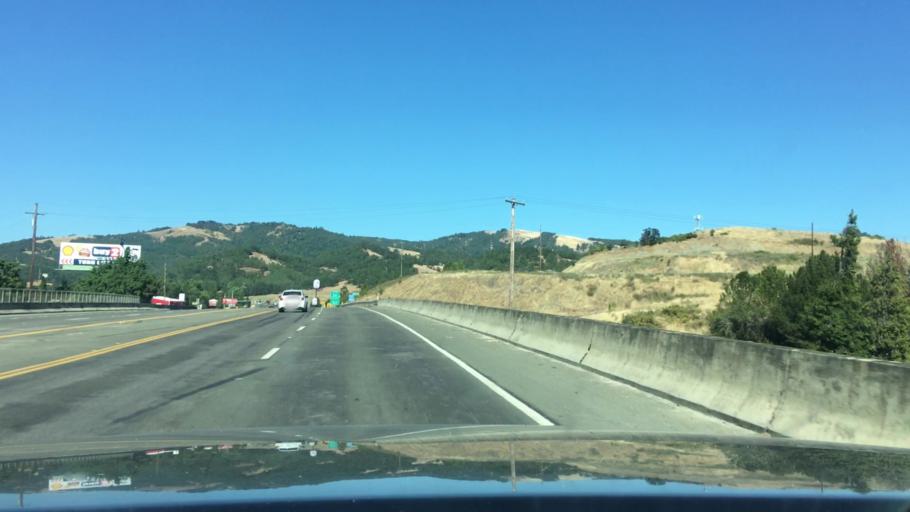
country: US
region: Oregon
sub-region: Douglas County
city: Green
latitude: 43.1475
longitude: -123.3763
